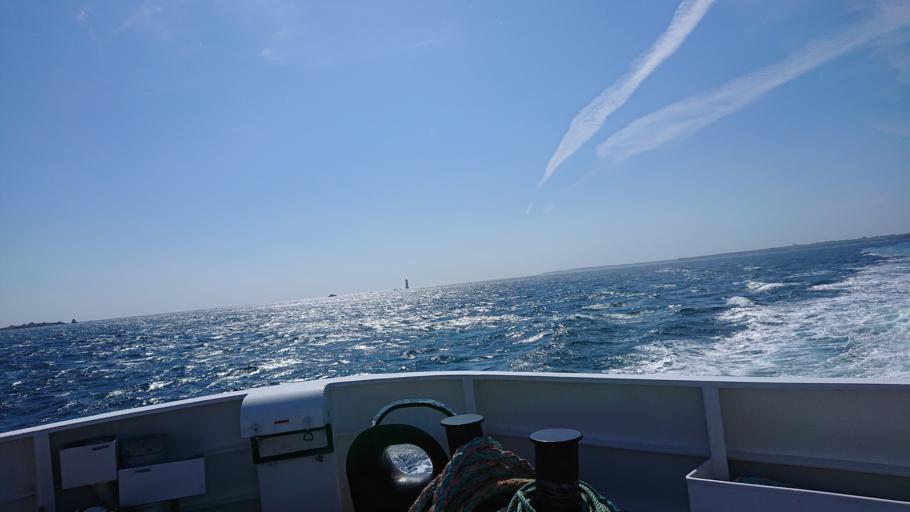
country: FR
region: Brittany
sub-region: Departement du Finistere
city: Lampaul-Plouarzel
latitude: 48.4450
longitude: -4.9931
